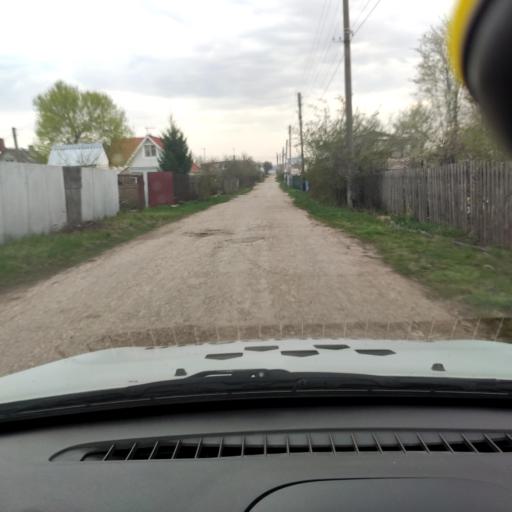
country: RU
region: Samara
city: Mezhdurechensk
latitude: 53.2462
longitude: 49.1477
